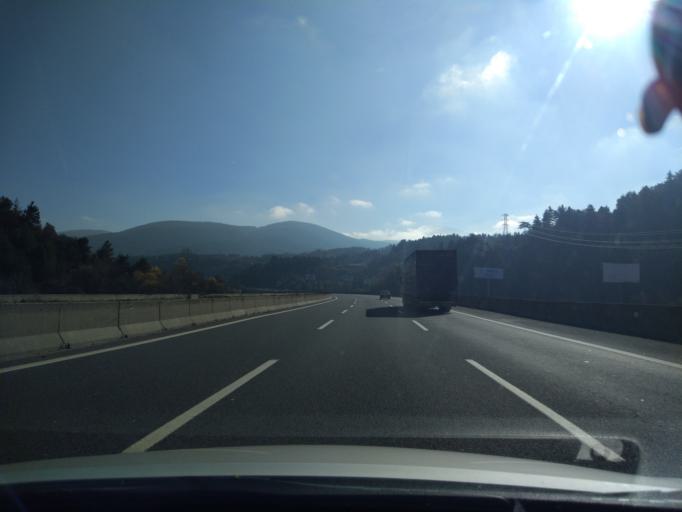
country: TR
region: Bolu
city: Bolu
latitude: 40.7448
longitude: 31.7824
